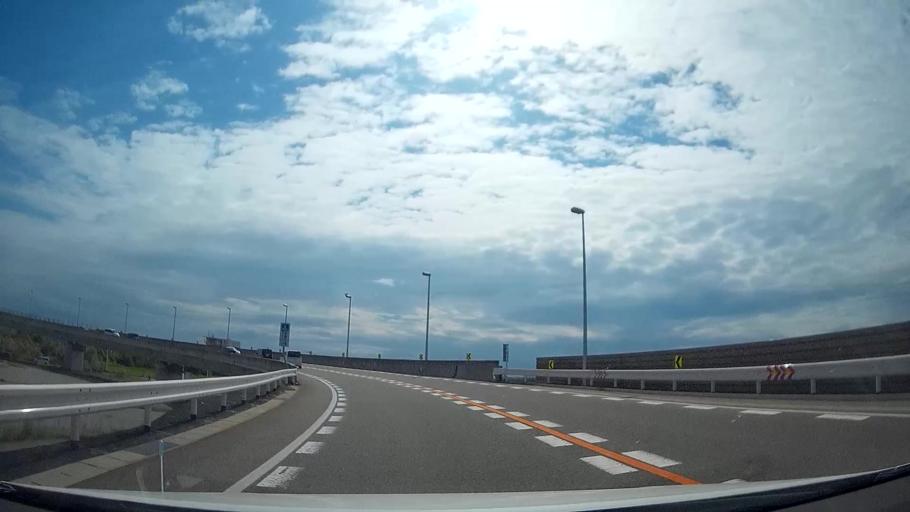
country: JP
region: Toyama
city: Nishishinminato
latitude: 36.7815
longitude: 137.1047
